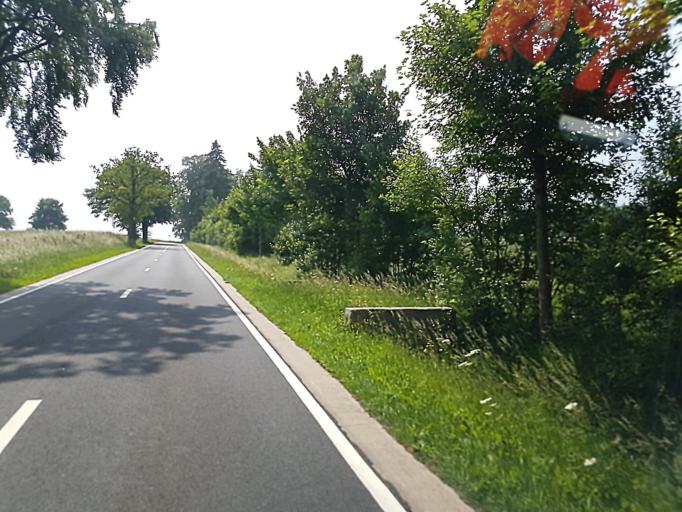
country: BE
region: Wallonia
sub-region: Province de Liege
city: Lierneux
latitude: 50.3350
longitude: 5.7850
